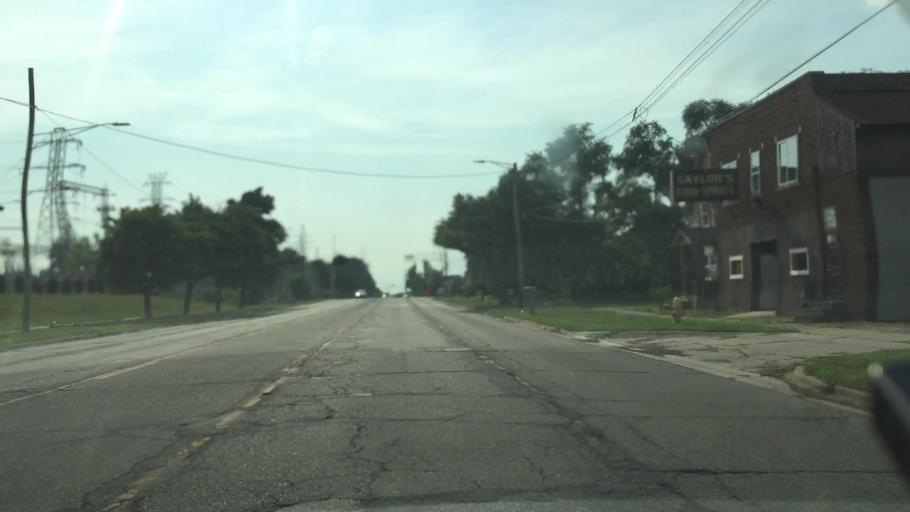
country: US
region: Michigan
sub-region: Oakland County
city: Pontiac
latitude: 42.6197
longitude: -83.2731
